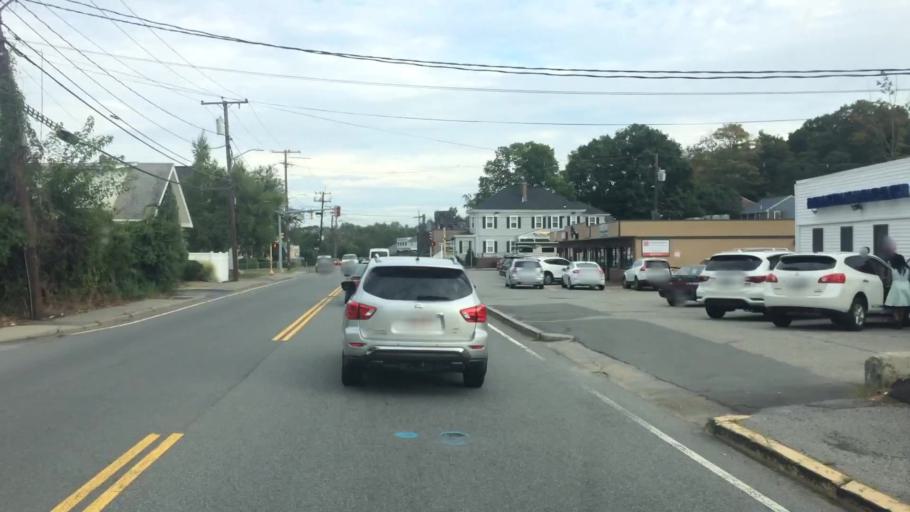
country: US
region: Massachusetts
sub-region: Middlesex County
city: Burlington
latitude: 42.4928
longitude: -71.1760
